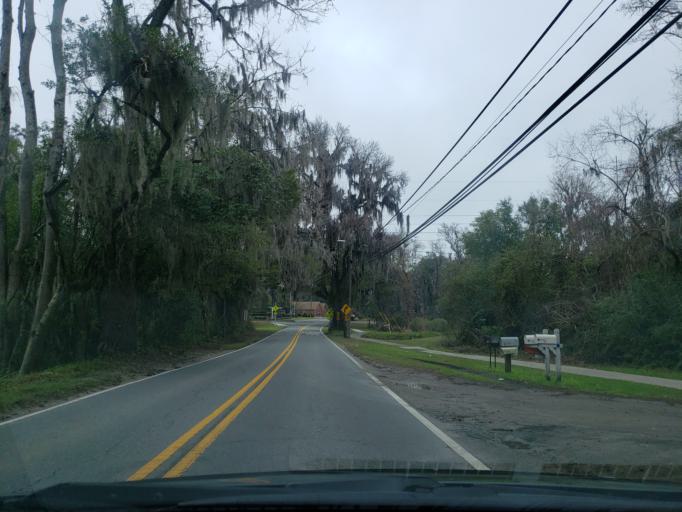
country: US
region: Georgia
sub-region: Chatham County
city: Montgomery
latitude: 31.9529
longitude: -81.1455
